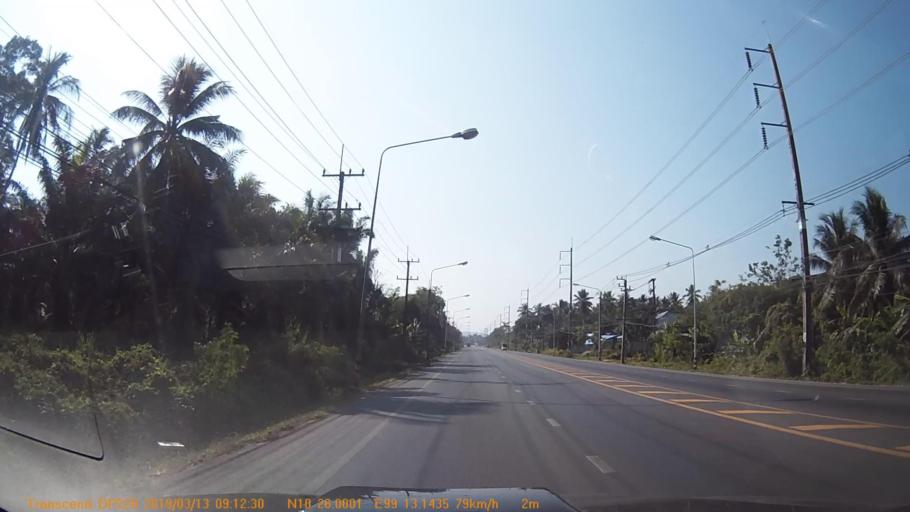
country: TH
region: Chumphon
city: Chumphon
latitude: 10.4331
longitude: 99.2192
